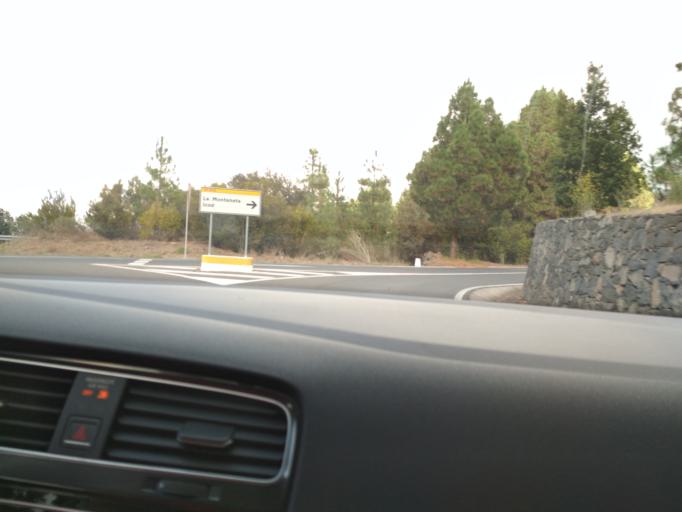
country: ES
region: Canary Islands
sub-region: Provincia de Santa Cruz de Tenerife
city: Santiago del Teide
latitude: 28.3288
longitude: -16.7827
